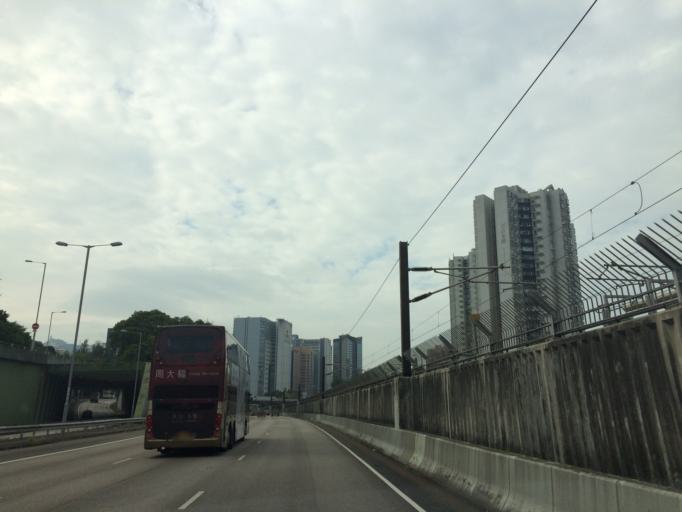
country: HK
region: Sha Tin
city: Sha Tin
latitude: 22.3976
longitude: 114.2112
